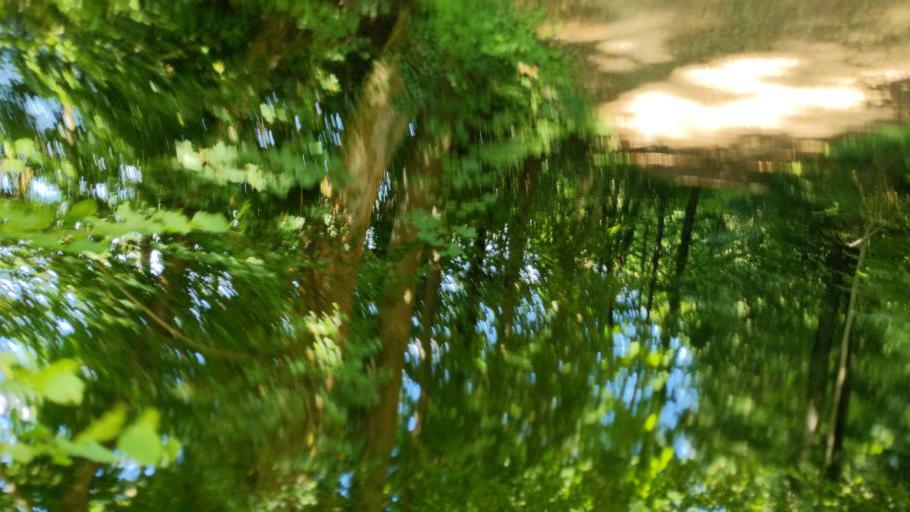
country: DE
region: Schleswig-Holstein
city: Schmilau
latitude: 53.6884
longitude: 10.7535
